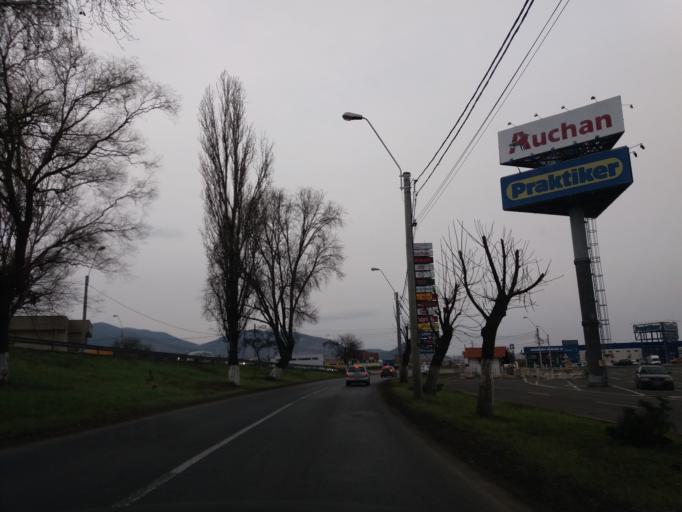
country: RO
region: Hunedoara
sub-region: Municipiul Deva
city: Deva
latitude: 45.8618
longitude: 22.9268
